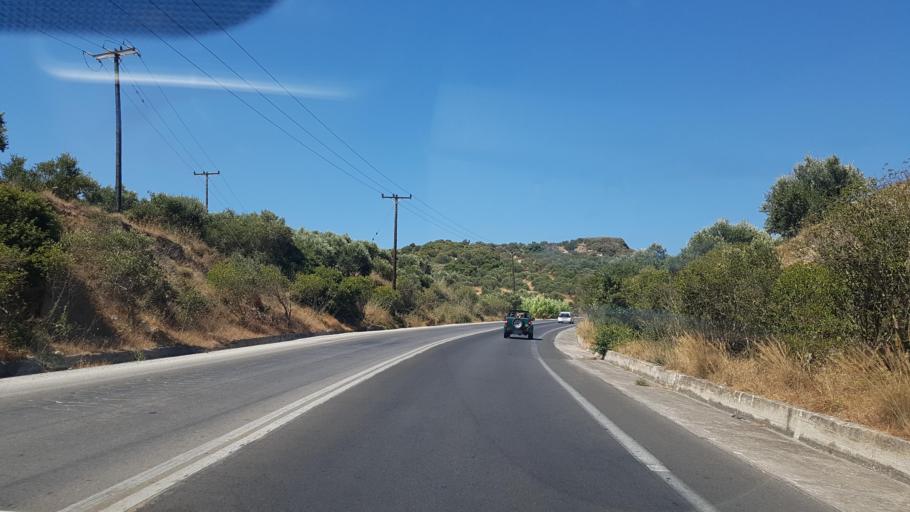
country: GR
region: Crete
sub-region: Nomos Chanias
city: Kolympari
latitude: 35.5284
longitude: 23.7608
